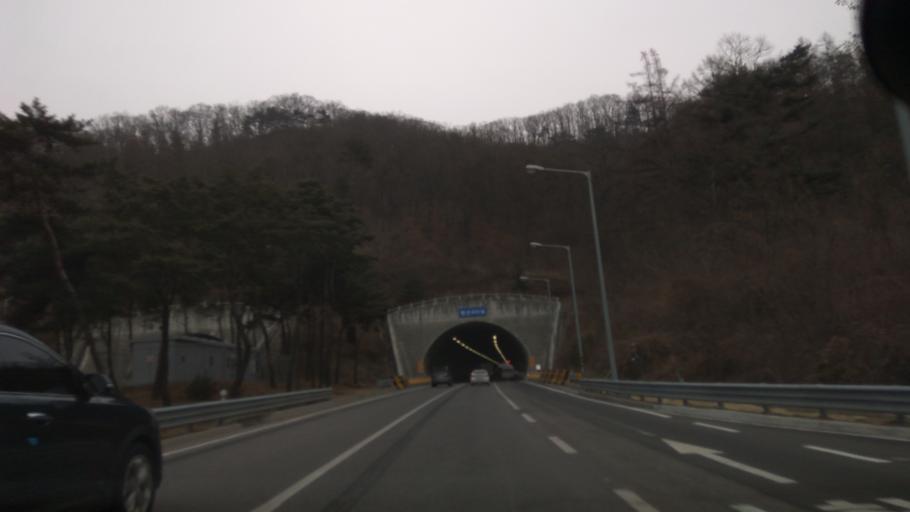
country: KR
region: Gangwon-do
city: Sindong
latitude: 37.7398
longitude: 127.6410
